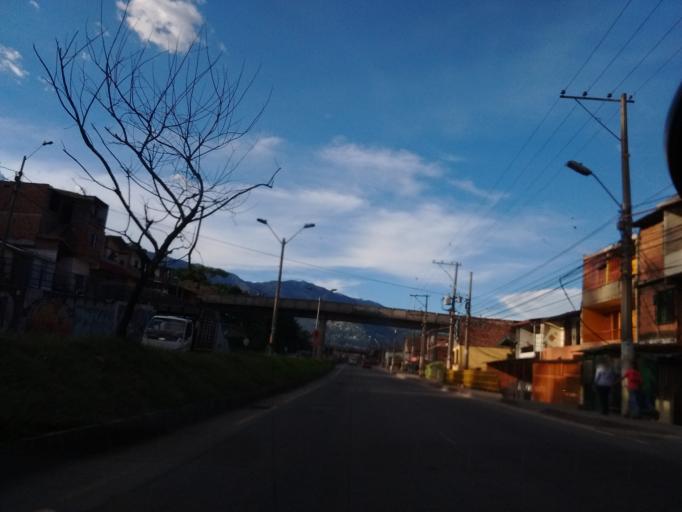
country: CO
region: Antioquia
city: Bello
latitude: 6.2985
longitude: -75.5597
